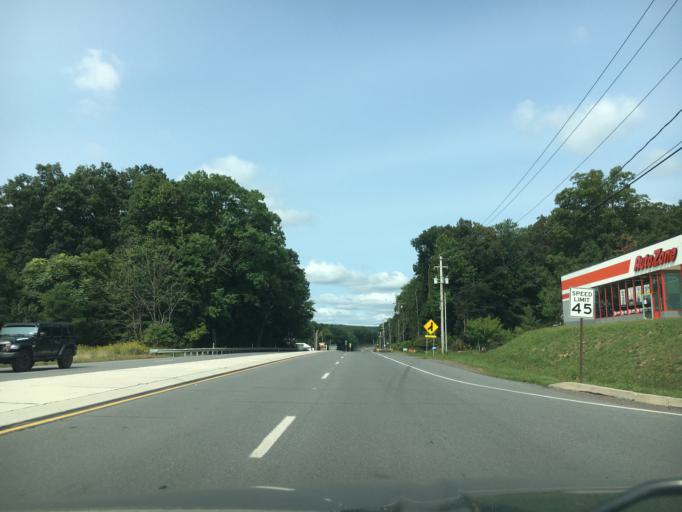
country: US
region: Pennsylvania
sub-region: Schuylkill County
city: Hometown
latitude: 40.8345
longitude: -75.9903
